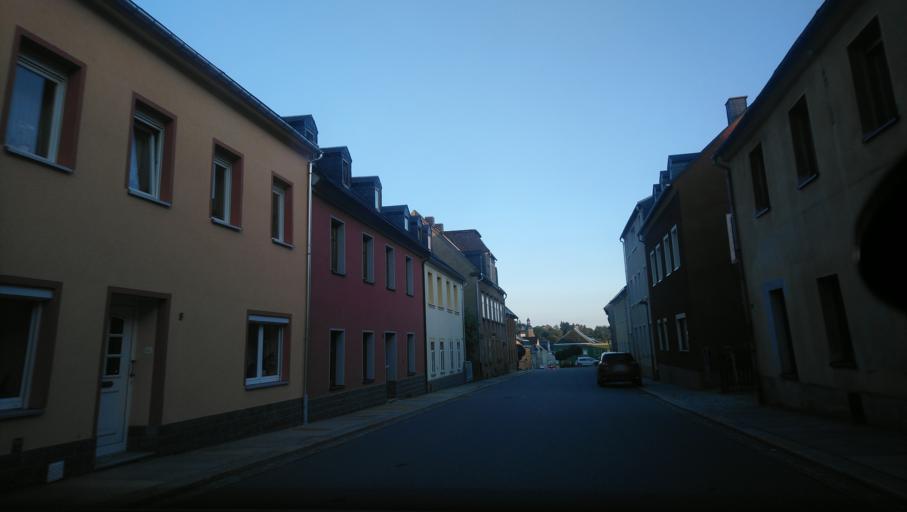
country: DE
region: Saxony
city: Geyer
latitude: 50.6275
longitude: 12.9187
